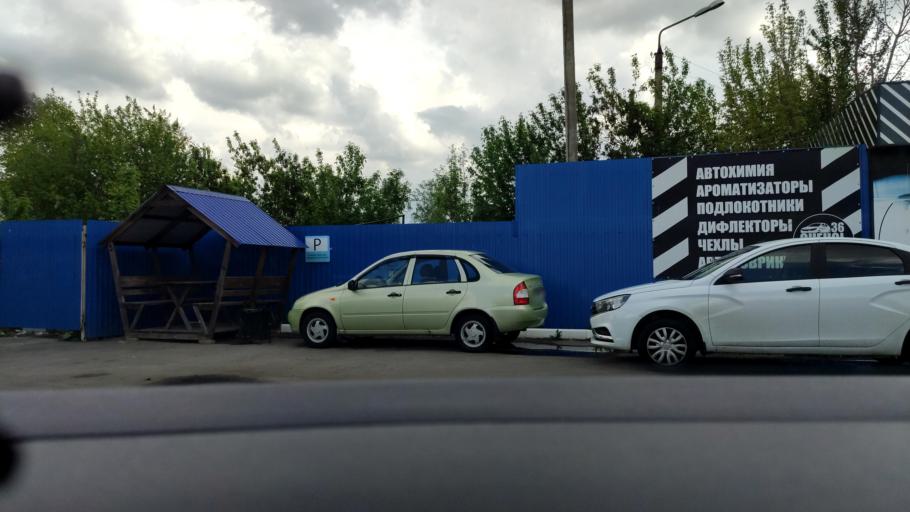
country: RU
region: Voronezj
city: Voronezh
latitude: 51.6538
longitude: 39.2948
